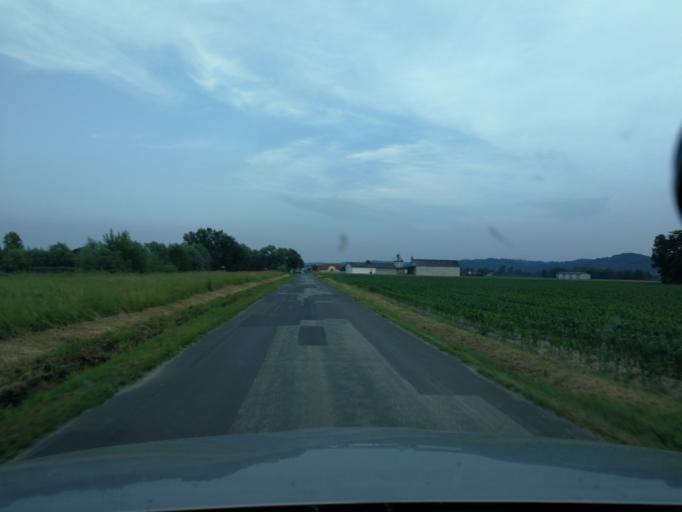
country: AT
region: Burgenland
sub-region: Politischer Bezirk Jennersdorf
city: Konigsdorf
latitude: 47.0096
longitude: 16.1583
